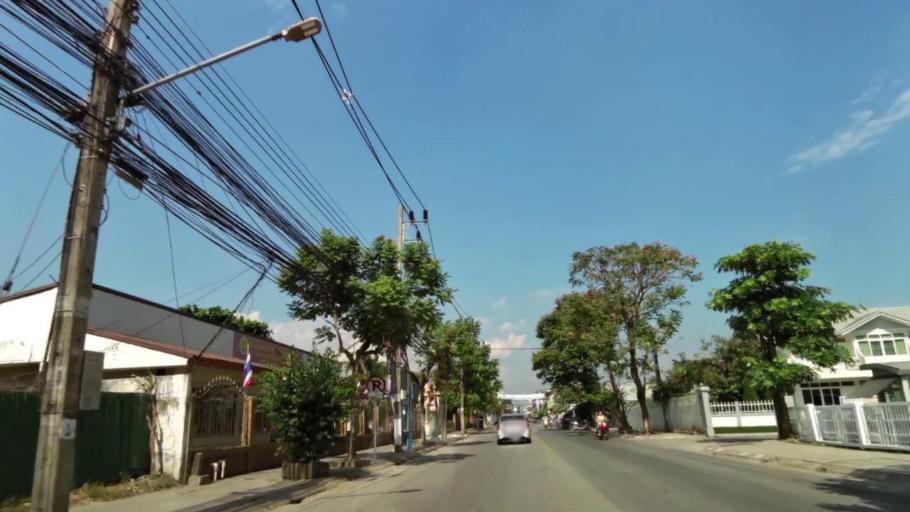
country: TH
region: Chiang Rai
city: Chiang Rai
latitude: 19.9026
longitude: 99.8283
